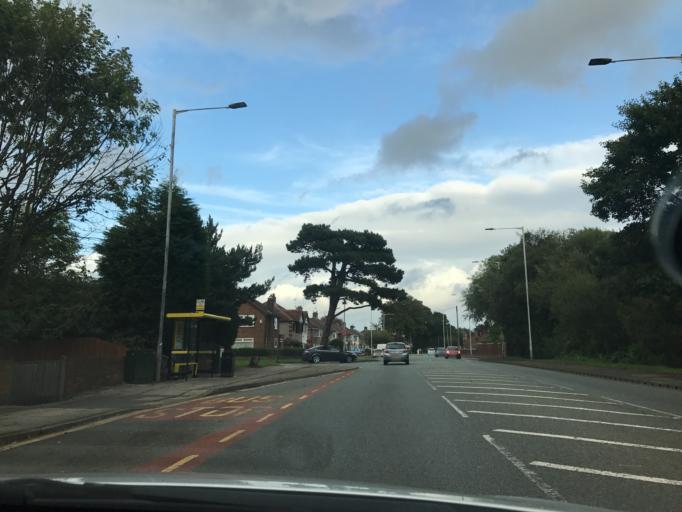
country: GB
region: England
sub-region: Metropolitan Borough of Wirral
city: Bebington
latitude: 53.3412
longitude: -3.0114
